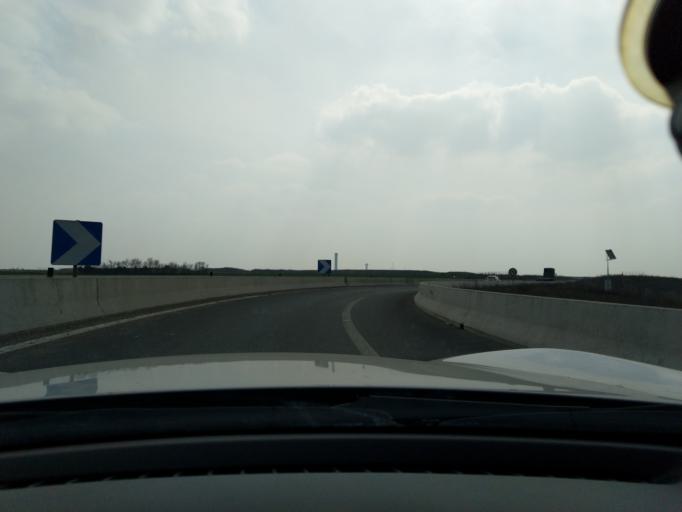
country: FR
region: Ile-de-France
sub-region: Departement du Val-d'Oise
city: Roissy-en-France
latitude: 49.0332
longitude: 2.5424
